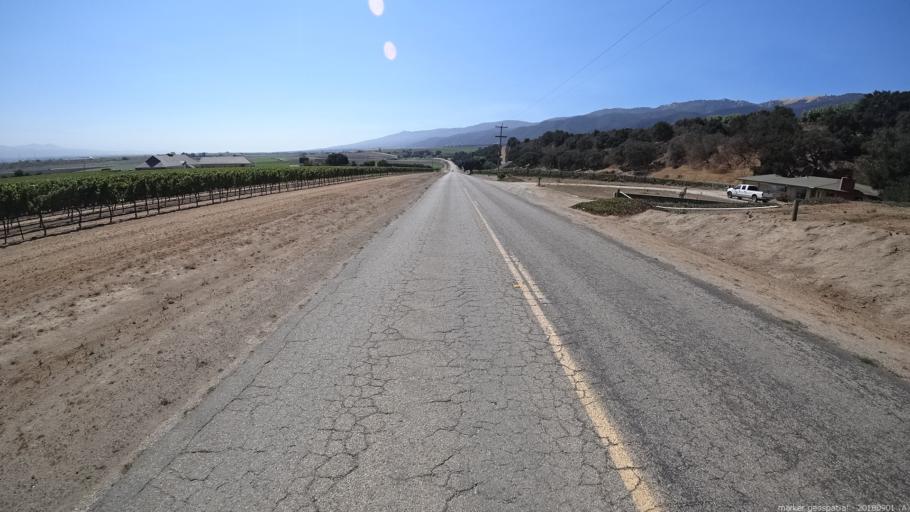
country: US
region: California
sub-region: Monterey County
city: Chualar
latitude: 36.5185
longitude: -121.5201
